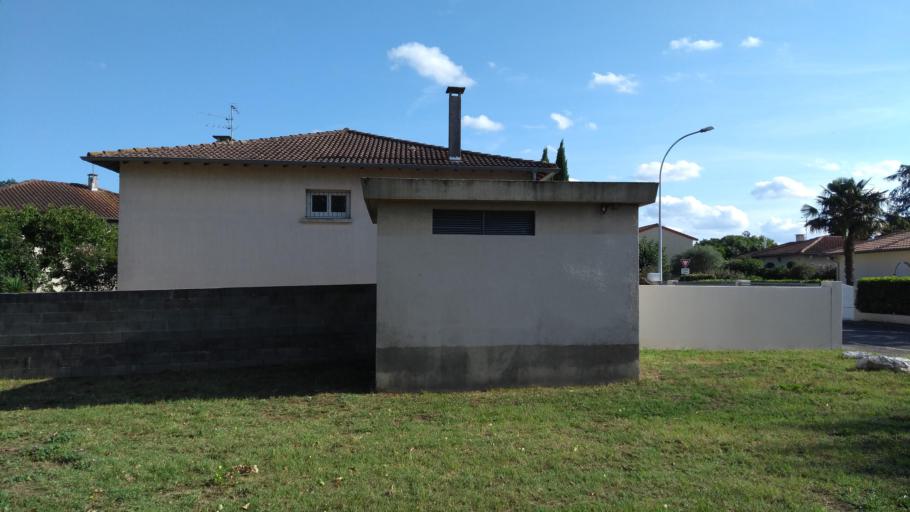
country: FR
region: Midi-Pyrenees
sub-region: Departement de la Haute-Garonne
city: Aucamville
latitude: 43.6729
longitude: 1.4327
